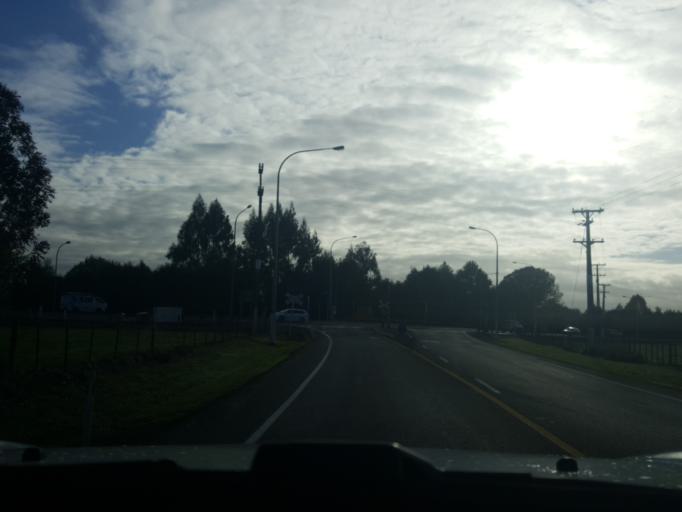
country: NZ
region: Waikato
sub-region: Waipa District
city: Cambridge
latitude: -37.6691
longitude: 175.4835
